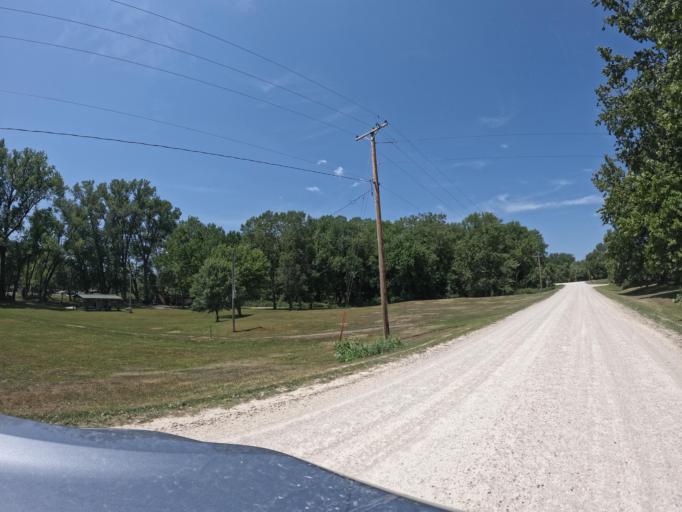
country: US
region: Iowa
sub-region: Henry County
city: Mount Pleasant
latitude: 40.9367
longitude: -91.6166
